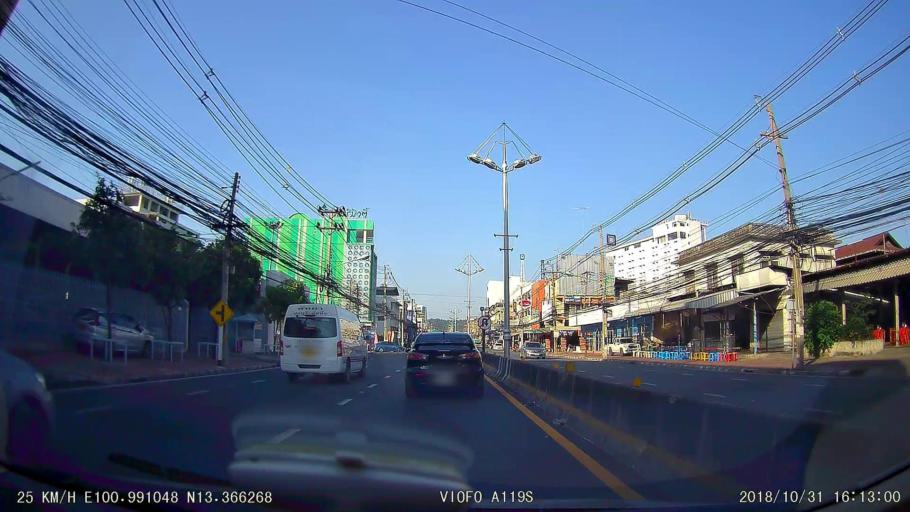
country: TH
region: Chon Buri
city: Chon Buri
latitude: 13.3664
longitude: 100.9911
